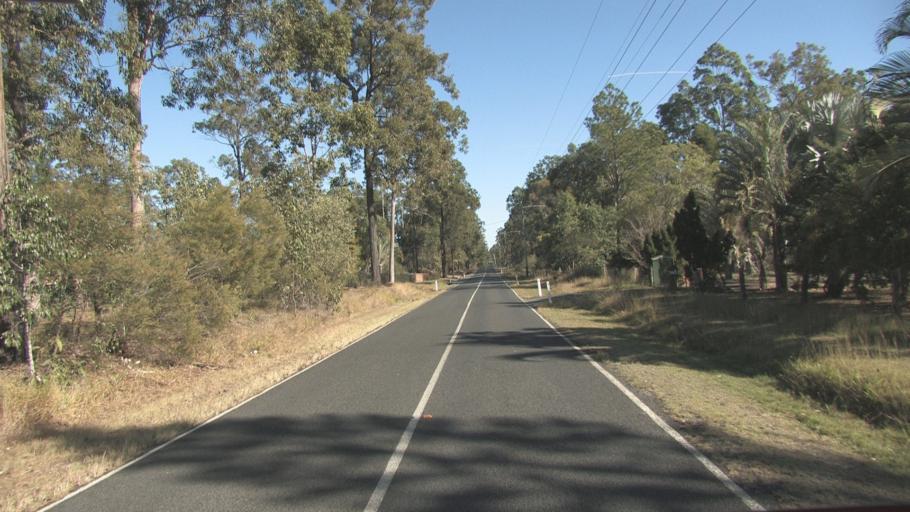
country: AU
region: Queensland
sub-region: Ipswich
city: Springfield Lakes
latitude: -27.6966
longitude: 152.9531
